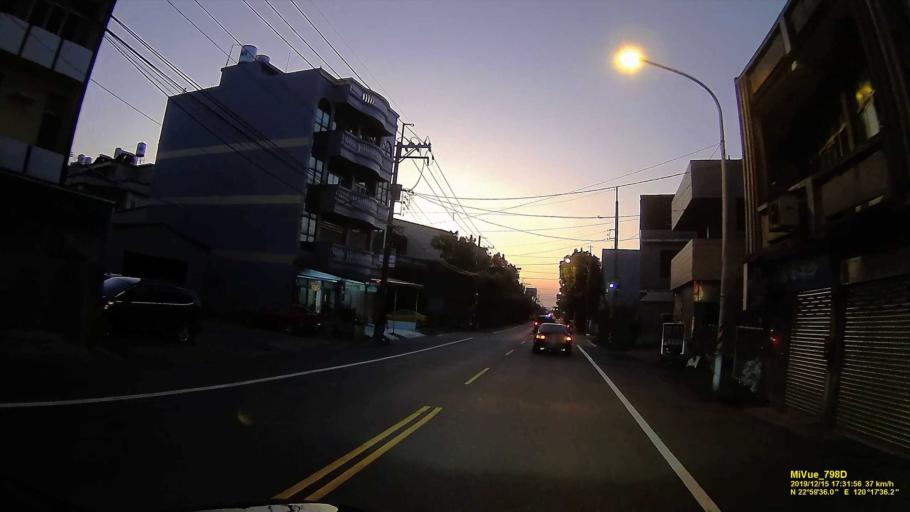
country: TW
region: Taiwan
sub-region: Tainan
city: Tainan
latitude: 22.9932
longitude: 120.2914
